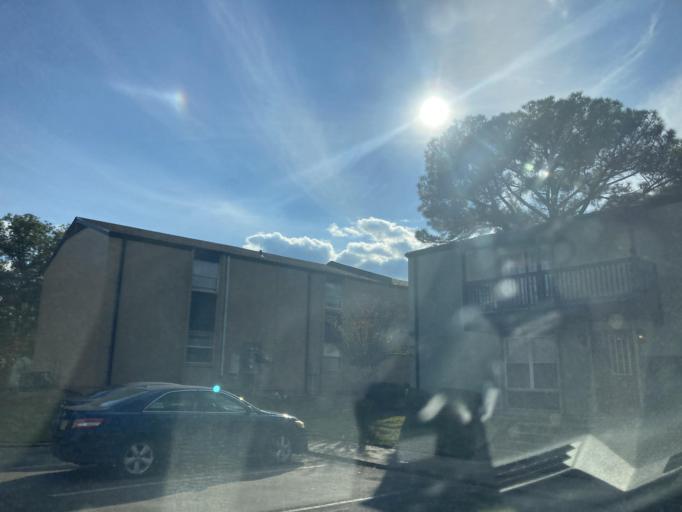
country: US
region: Mississippi
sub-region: Lamar County
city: West Hattiesburg
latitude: 31.3214
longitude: -89.3542
